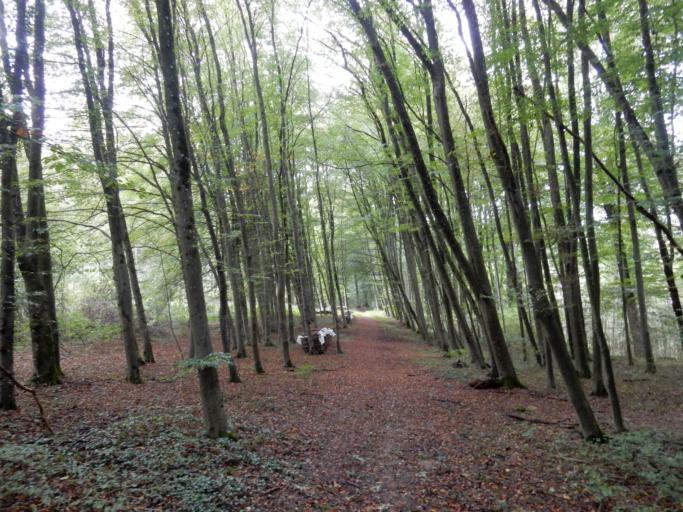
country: LU
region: Luxembourg
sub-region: Canton de Capellen
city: Kehlen
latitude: 49.6913
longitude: 6.0211
